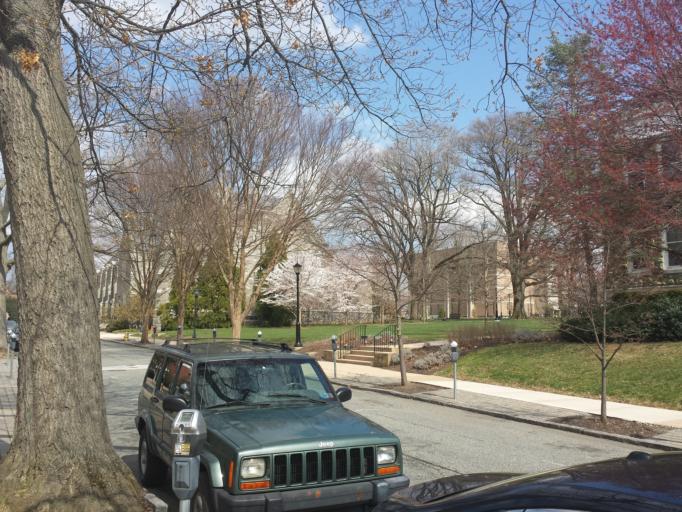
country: US
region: Pennsylvania
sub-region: Chester County
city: West Chester
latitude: 39.9531
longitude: -75.5996
